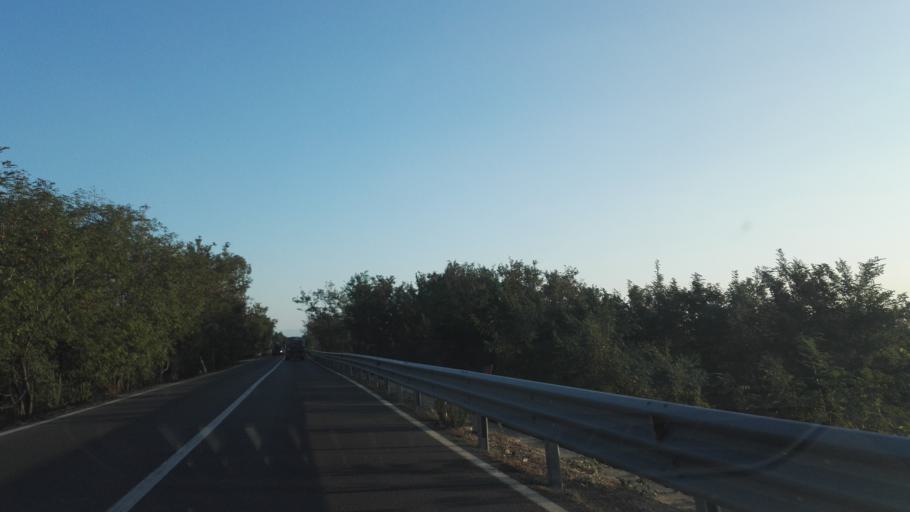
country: IT
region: Calabria
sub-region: Provincia di Catanzaro
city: Santa Caterina dello Ionio Marina
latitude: 38.5489
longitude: 16.5702
